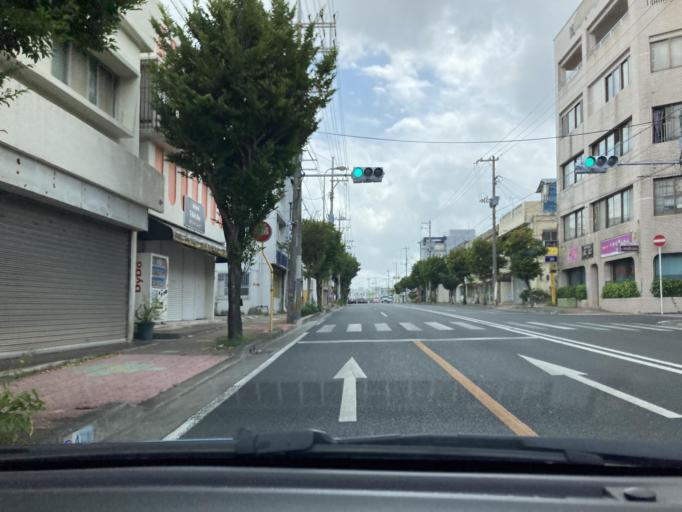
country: JP
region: Okinawa
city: Okinawa
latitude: 26.3370
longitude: 127.8167
